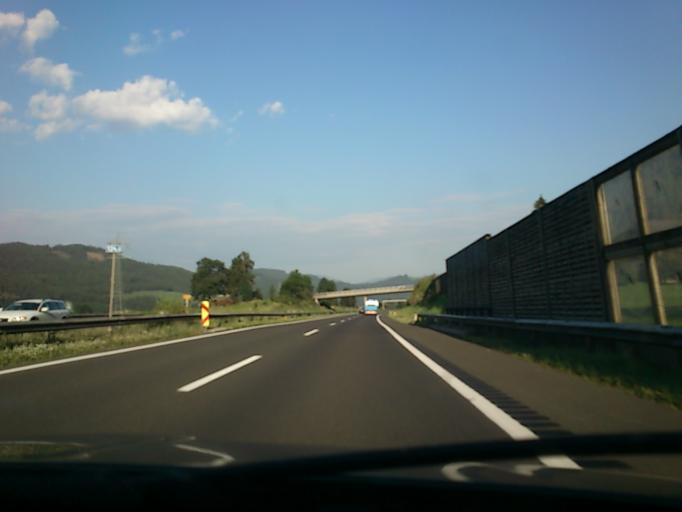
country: AT
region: Styria
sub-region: Politischer Bezirk Leoben
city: Kammern im Liesingtal
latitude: 47.3829
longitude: 14.9346
